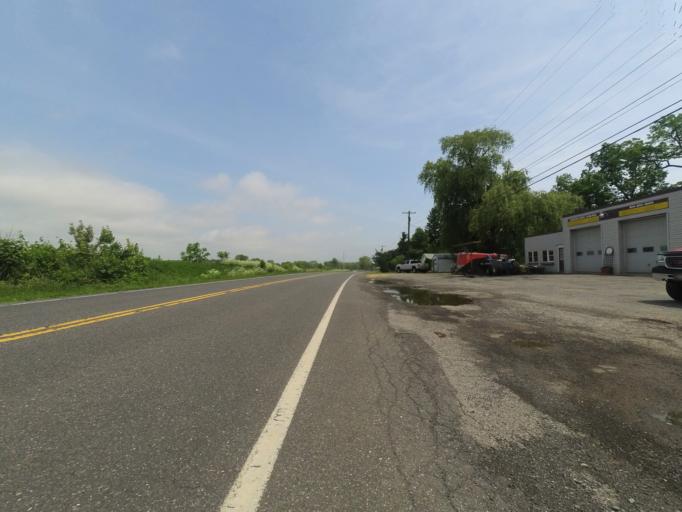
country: US
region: Pennsylvania
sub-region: Centre County
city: Pine Grove Mills
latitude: 40.7109
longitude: -77.9638
